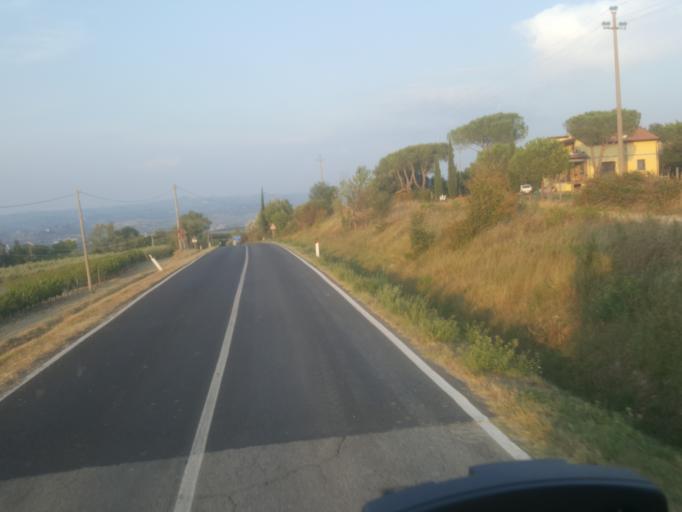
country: IT
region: Tuscany
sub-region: Province of Florence
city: Gambassi Terme
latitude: 43.5449
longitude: 10.9771
